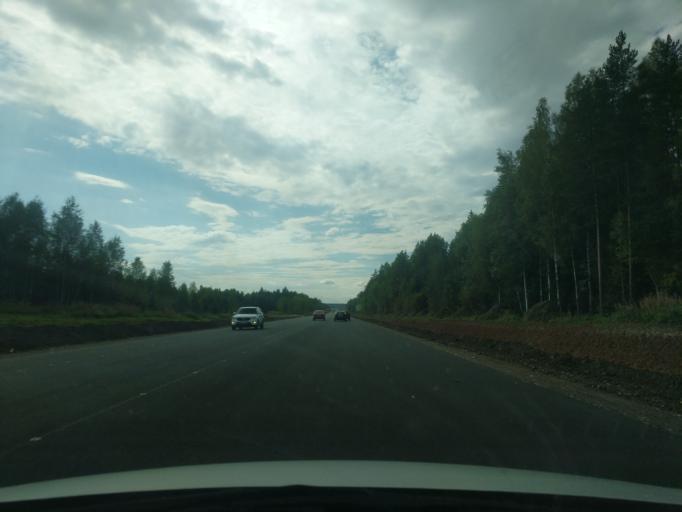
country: RU
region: Kostroma
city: Sudislavl'
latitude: 57.8230
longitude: 41.4948
